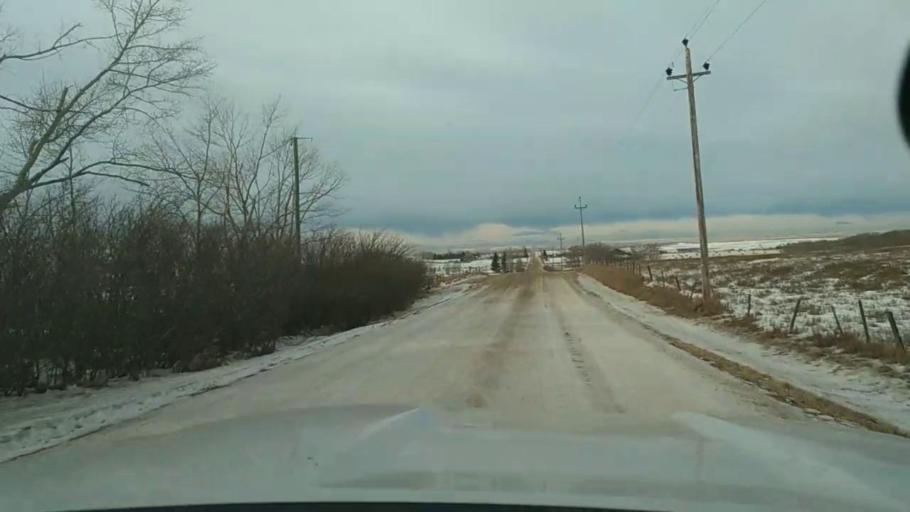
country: CA
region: Alberta
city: Airdrie
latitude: 51.2417
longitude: -113.9202
